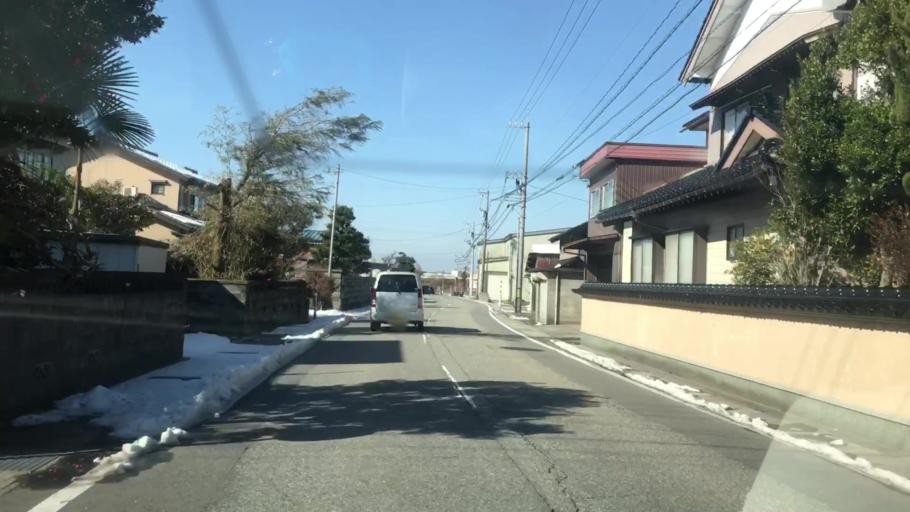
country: JP
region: Toyama
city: Toyama-shi
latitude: 36.6470
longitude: 137.2491
